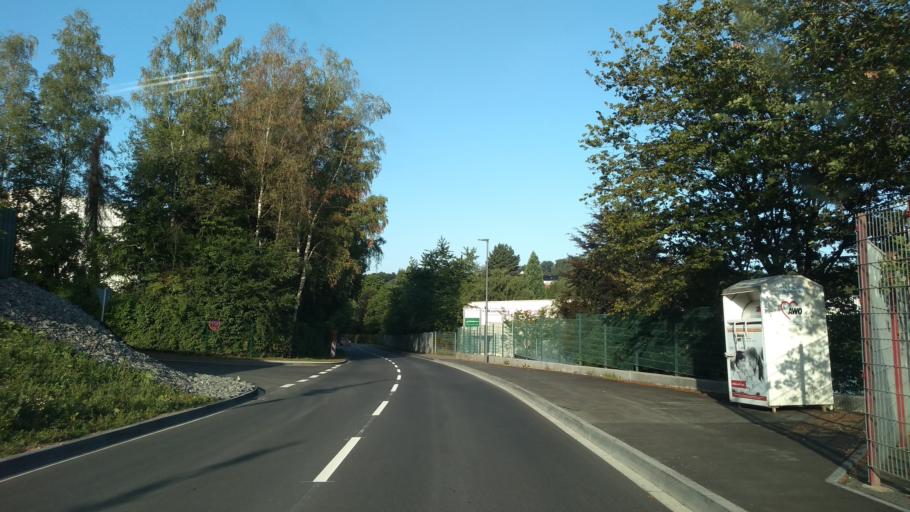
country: DE
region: North Rhine-Westphalia
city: Wiehl
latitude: 50.9693
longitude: 7.5170
